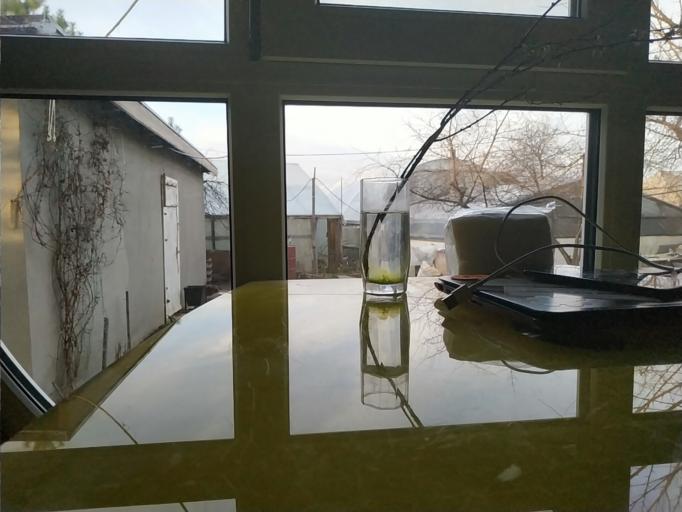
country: RU
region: Republic of Karelia
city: Suoyarvi
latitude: 62.2605
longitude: 32.0906
